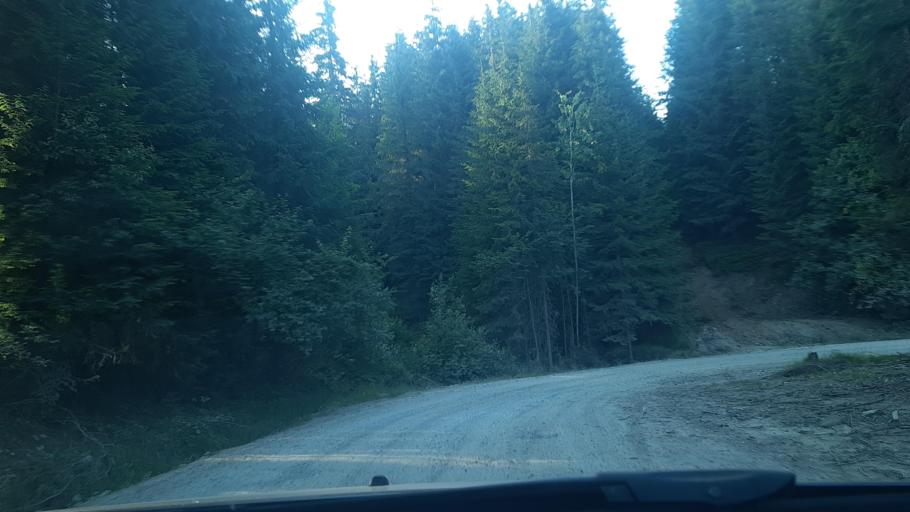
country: RO
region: Alba
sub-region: Comuna Sugag
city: Sugag
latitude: 45.5808
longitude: 23.6075
